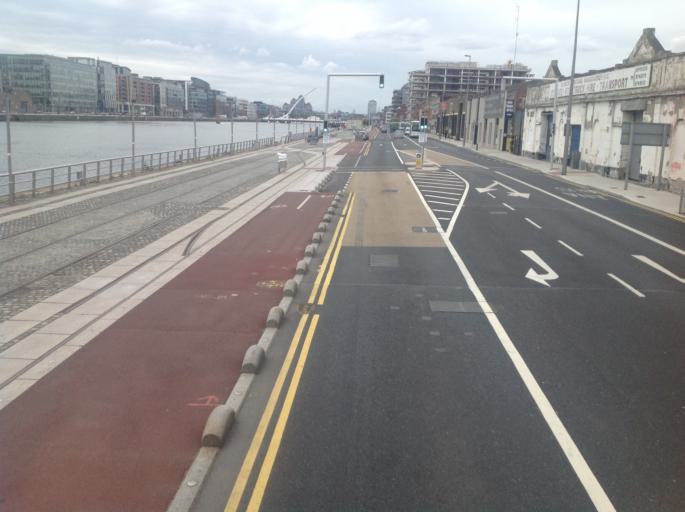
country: IE
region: Leinster
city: Ringsend
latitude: 53.3468
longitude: -6.2290
